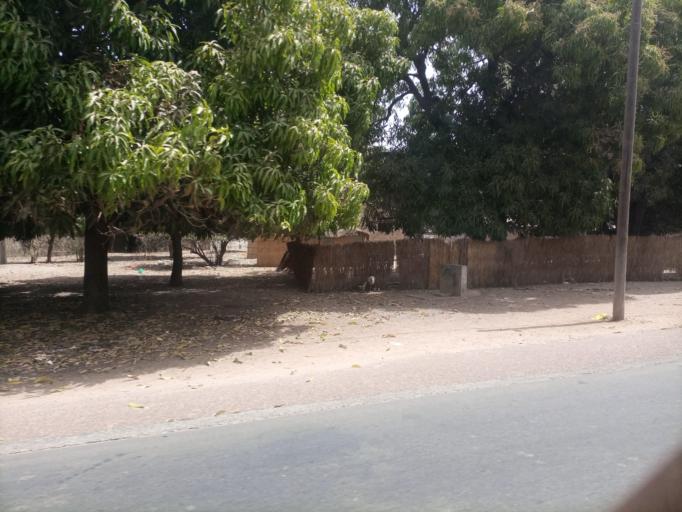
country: SN
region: Fatick
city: Sokone
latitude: 13.7447
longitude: -16.4318
